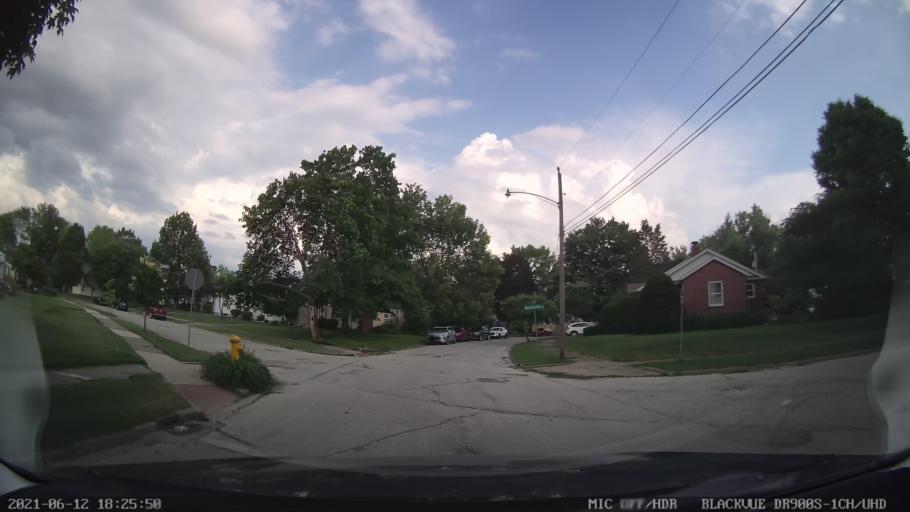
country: US
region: Illinois
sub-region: McLean County
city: Bloomington
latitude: 40.4738
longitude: -88.9744
